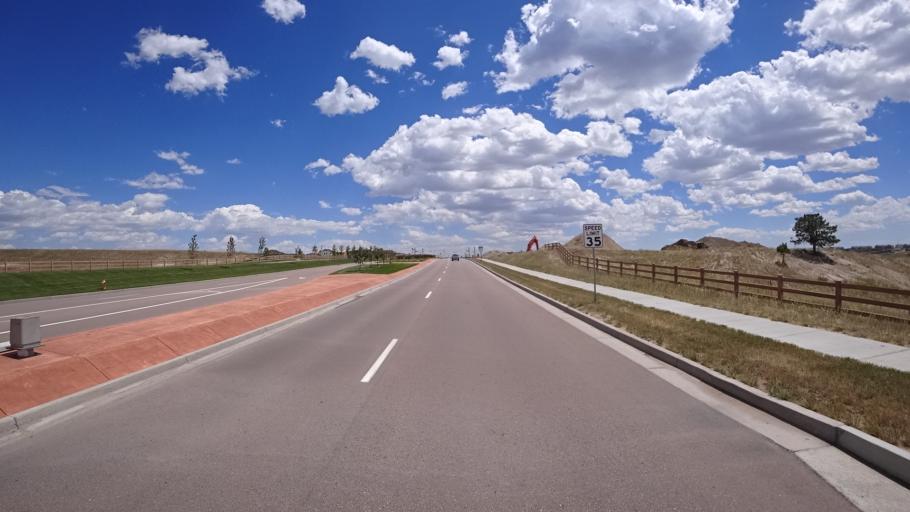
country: US
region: Colorado
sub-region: El Paso County
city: Black Forest
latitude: 38.9607
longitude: -104.7111
